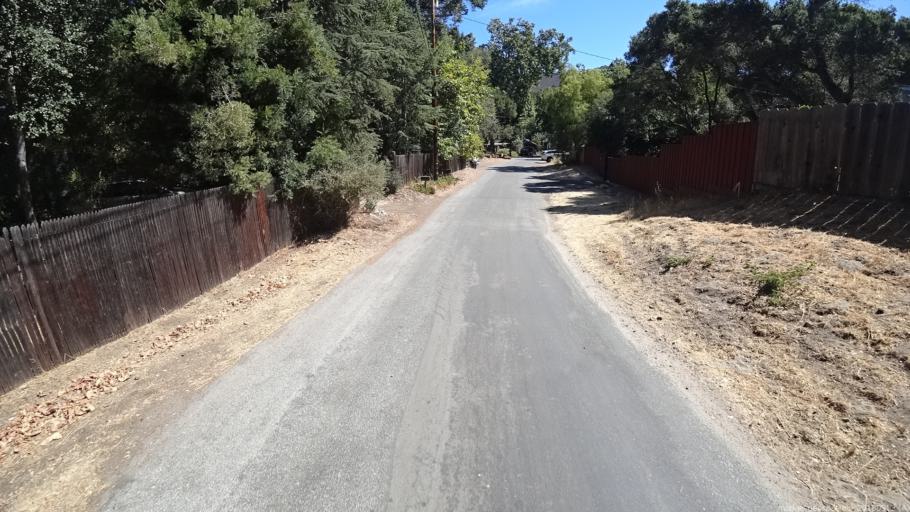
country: US
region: California
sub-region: Monterey County
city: Carmel Valley Village
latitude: 36.4744
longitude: -121.7217
